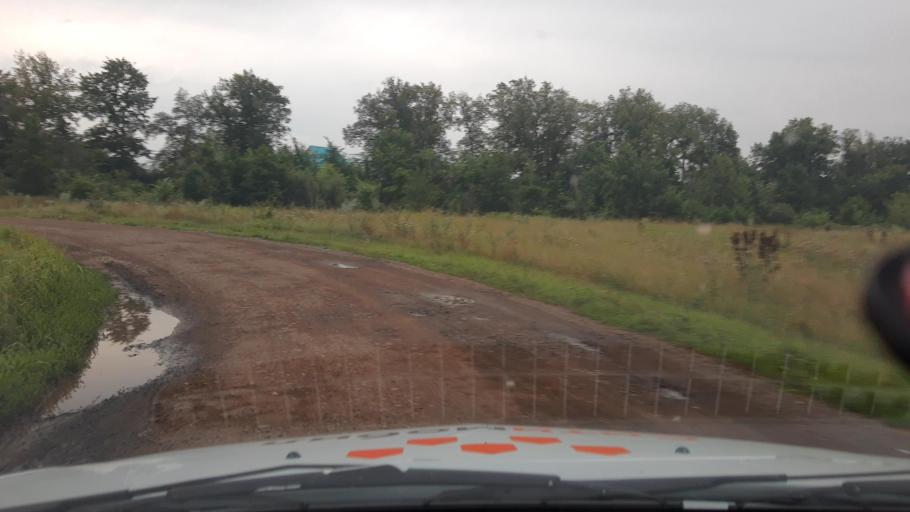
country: RU
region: Bashkortostan
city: Ufa
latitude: 54.5693
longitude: 55.9485
